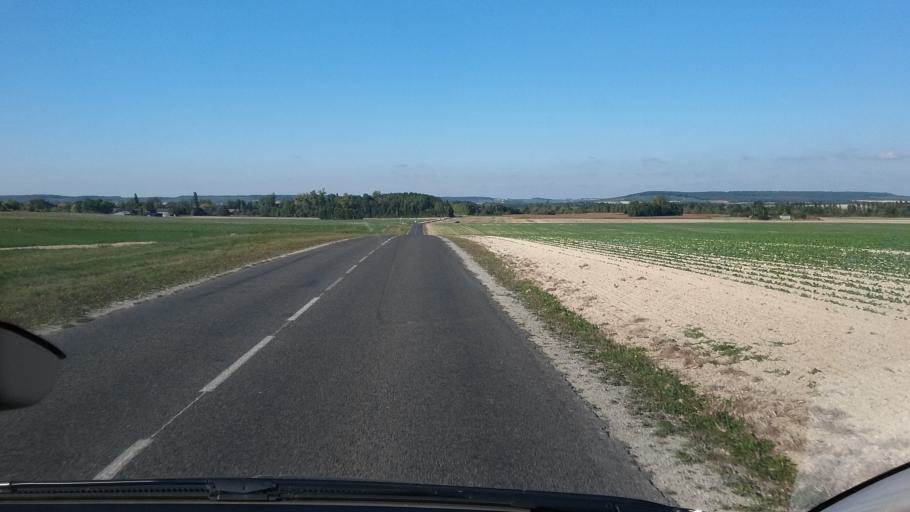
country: FR
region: Champagne-Ardenne
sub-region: Departement de la Marne
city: Connantre
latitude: 48.7807
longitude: 3.8637
